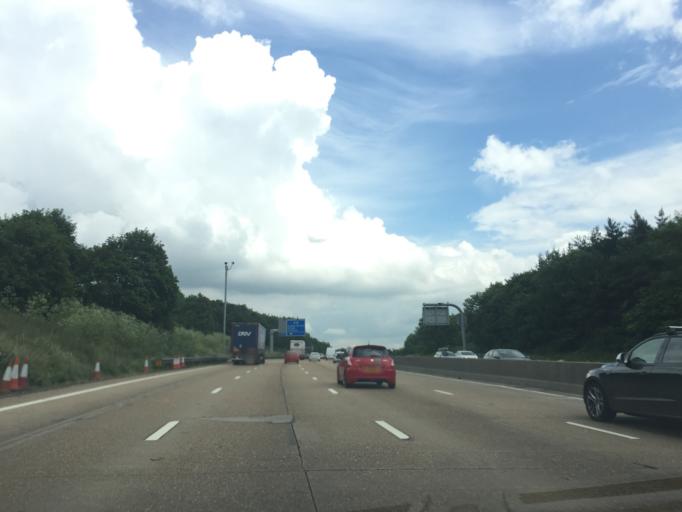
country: GB
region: England
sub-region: Hertfordshire
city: Cuffley
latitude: 51.6896
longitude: -0.0866
